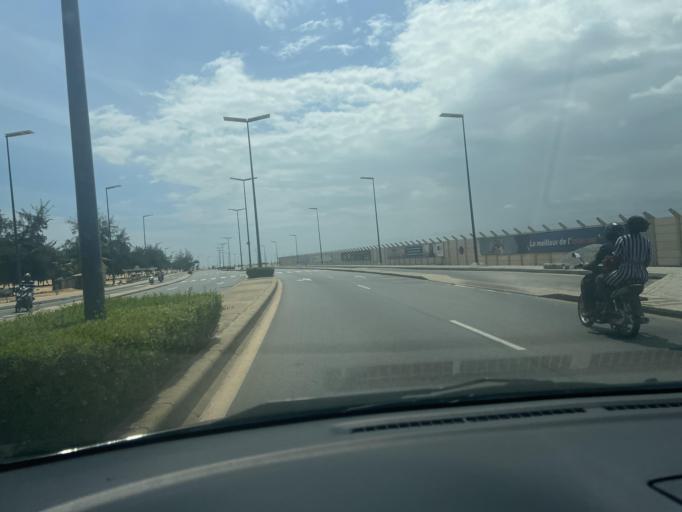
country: BJ
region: Littoral
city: Cotonou
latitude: 6.3497
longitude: 2.3795
